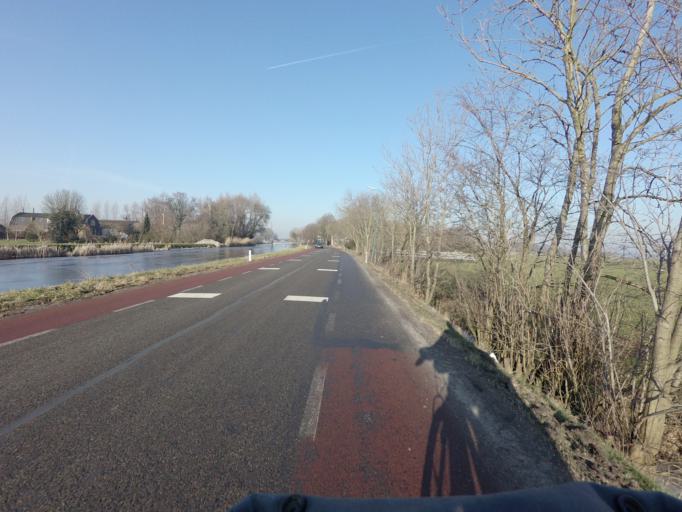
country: NL
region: Utrecht
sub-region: Stichtse Vecht
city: Vreeland
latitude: 52.2522
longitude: 4.9937
